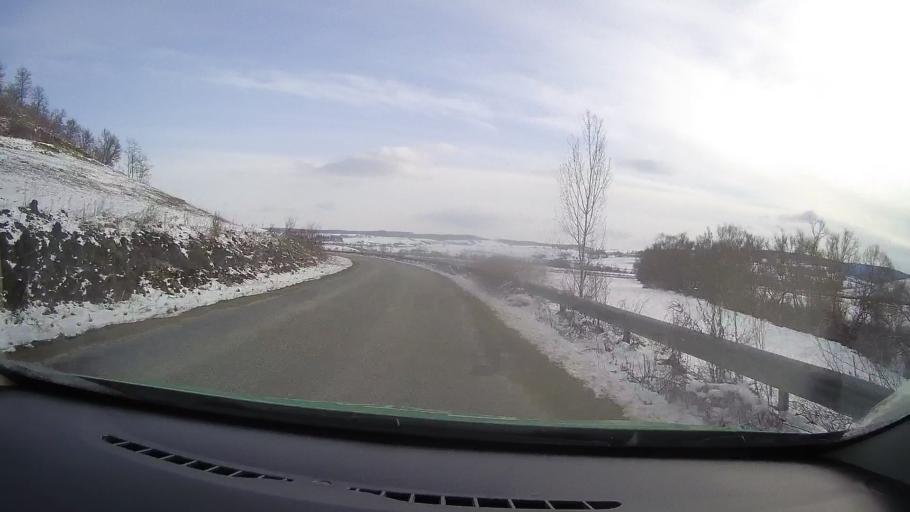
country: RO
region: Sibiu
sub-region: Comuna Merghindeal
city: Merghindeal
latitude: 45.9796
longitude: 24.7005
